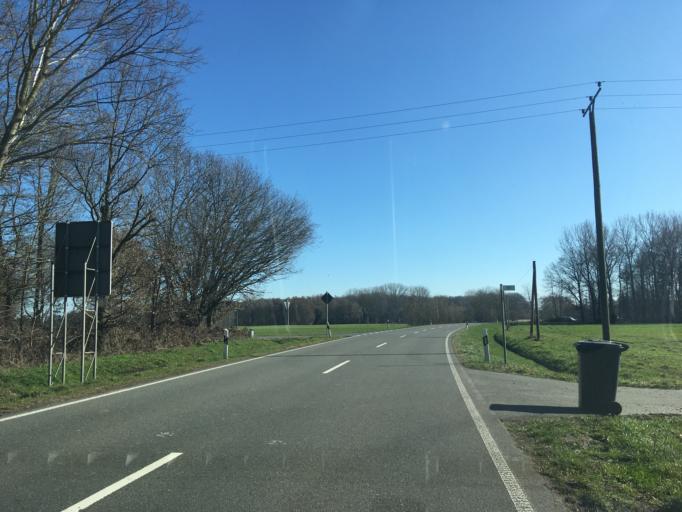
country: DE
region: North Rhine-Westphalia
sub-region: Regierungsbezirk Munster
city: Rhede
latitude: 51.8561
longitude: 6.7716
